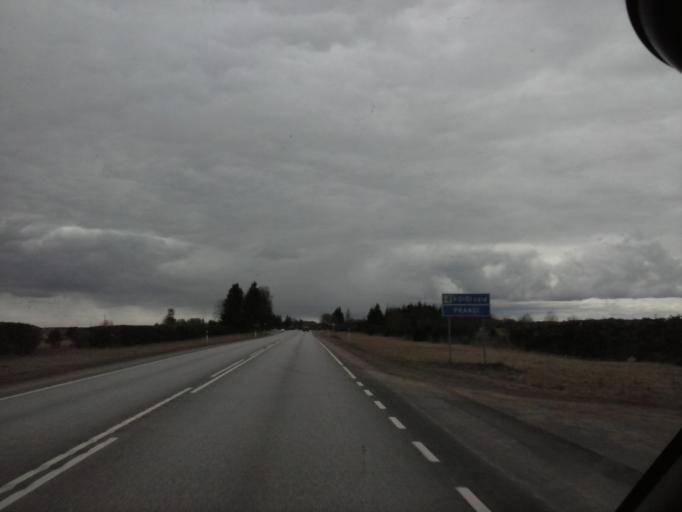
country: EE
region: Jaervamaa
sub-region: Paide linn
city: Paide
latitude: 58.8549
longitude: 25.7226
